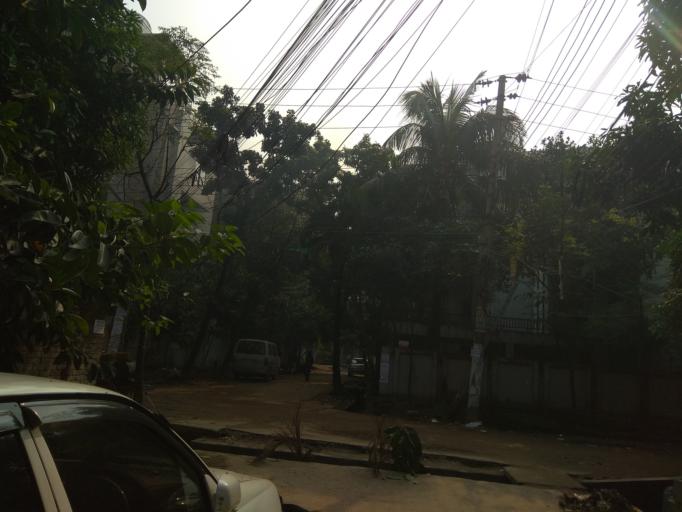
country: BD
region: Dhaka
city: Tungi
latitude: 23.8730
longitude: 90.3993
